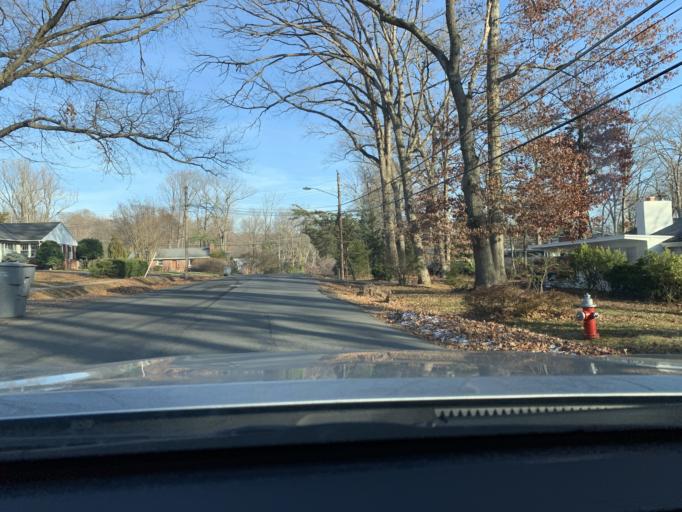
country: US
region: Virginia
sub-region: Fairfax County
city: Jefferson
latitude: 38.8491
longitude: -77.1773
